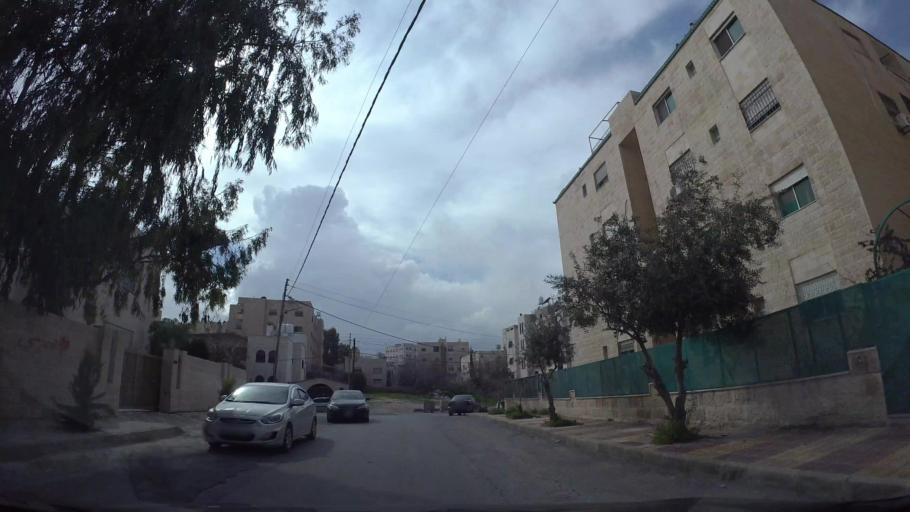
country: JO
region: Amman
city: Amman
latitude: 32.0078
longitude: 35.9394
